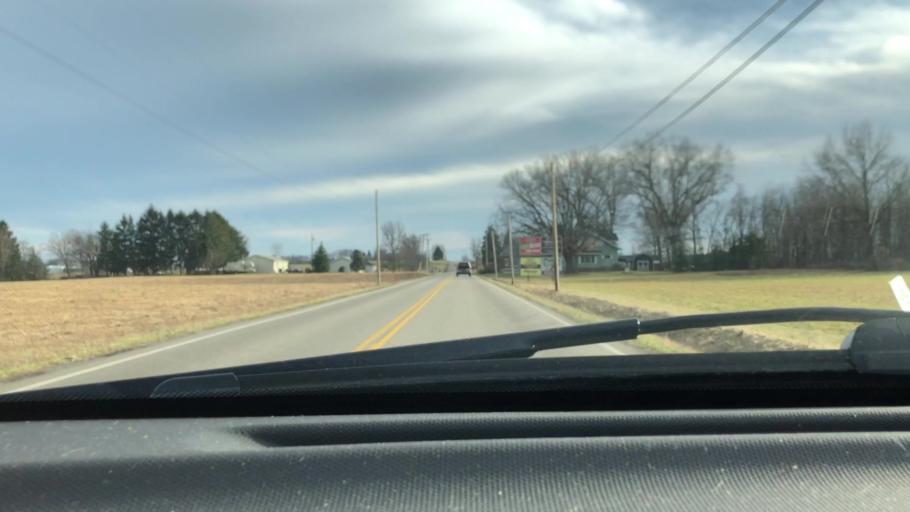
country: US
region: Ohio
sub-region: Wayne County
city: Dalton
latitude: 40.7807
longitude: -81.7453
